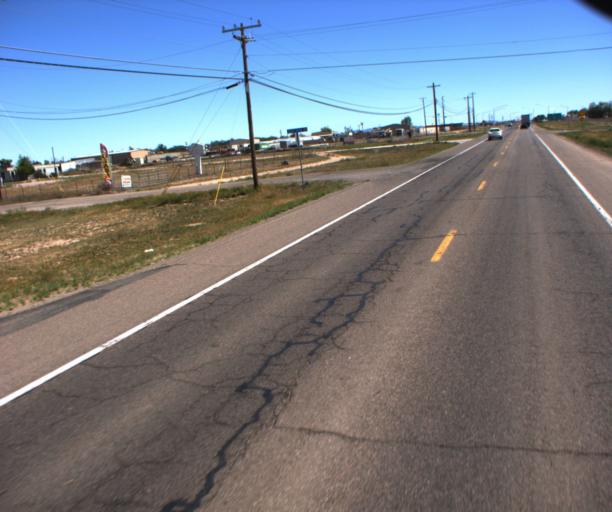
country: US
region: Arizona
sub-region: Yavapai County
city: Chino Valley
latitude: 34.7934
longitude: -112.4514
